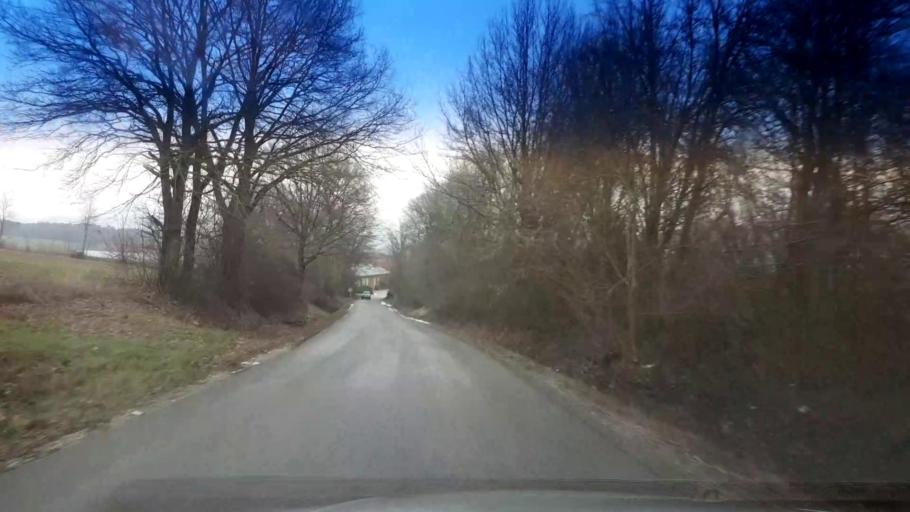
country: DE
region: Bavaria
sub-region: Upper Franconia
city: Hallerndorf
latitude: 49.7736
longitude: 10.9915
